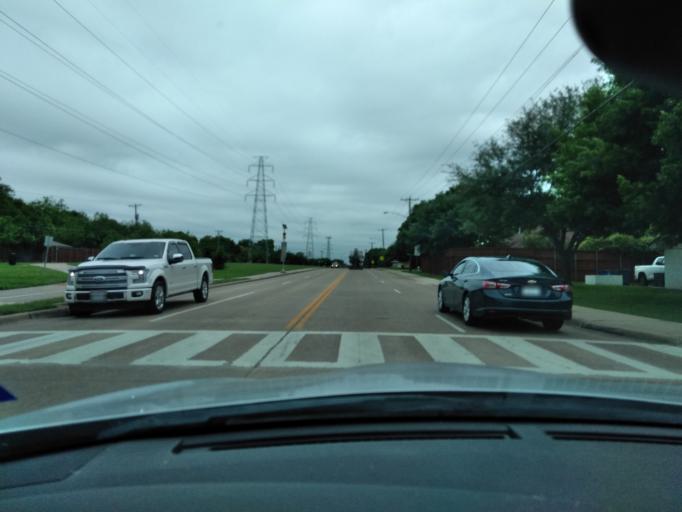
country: US
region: Texas
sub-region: Dallas County
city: Richardson
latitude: 32.9558
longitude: -96.7786
